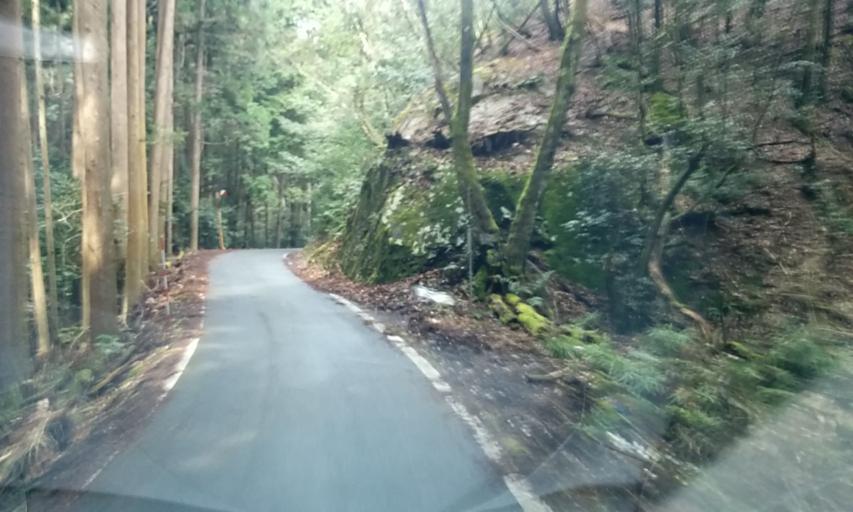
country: JP
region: Kyoto
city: Kameoka
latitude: 35.1153
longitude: 135.4309
